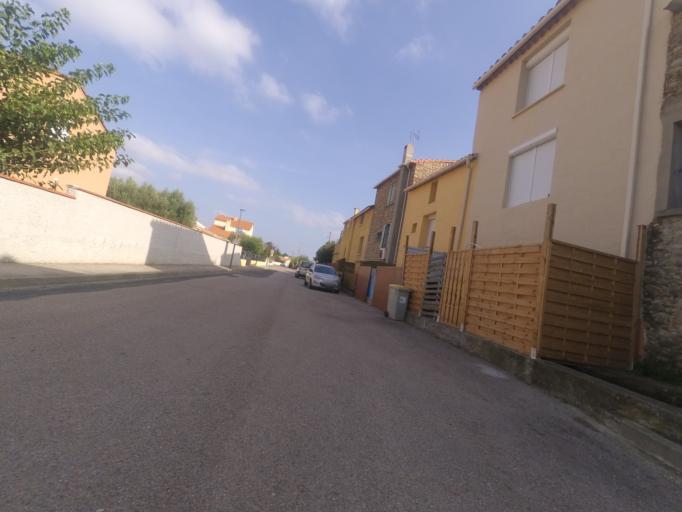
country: FR
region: Languedoc-Roussillon
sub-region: Departement des Pyrenees-Orientales
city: Corneilla-la-Riviere
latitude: 42.6964
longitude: 2.7312
